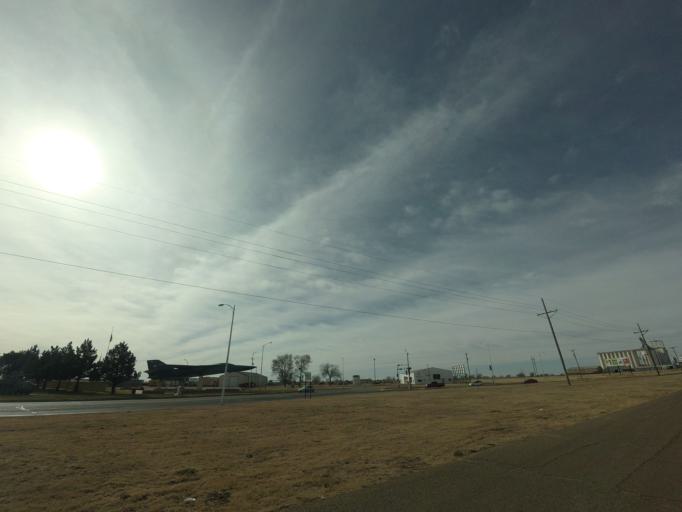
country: US
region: New Mexico
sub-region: Curry County
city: Clovis
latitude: 34.4047
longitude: -103.2458
